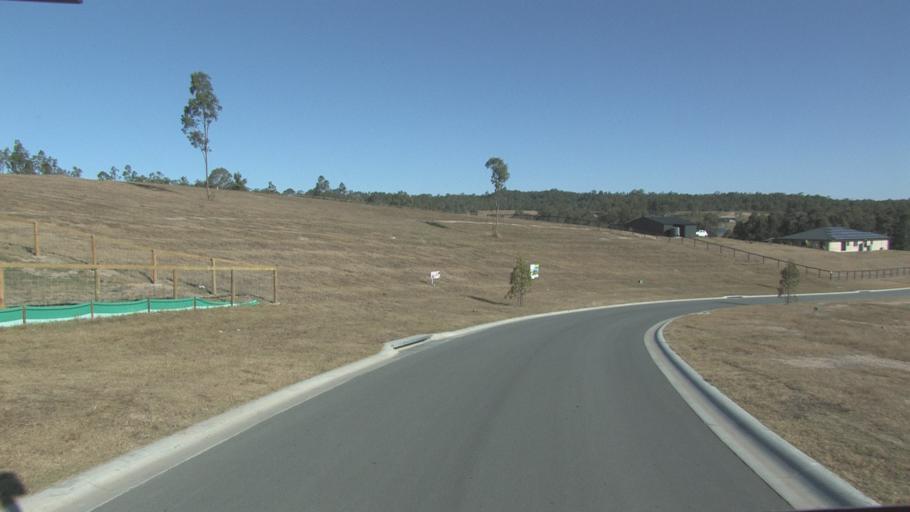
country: AU
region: Queensland
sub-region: Logan
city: Cedar Vale
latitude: -27.8729
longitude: 153.0518
